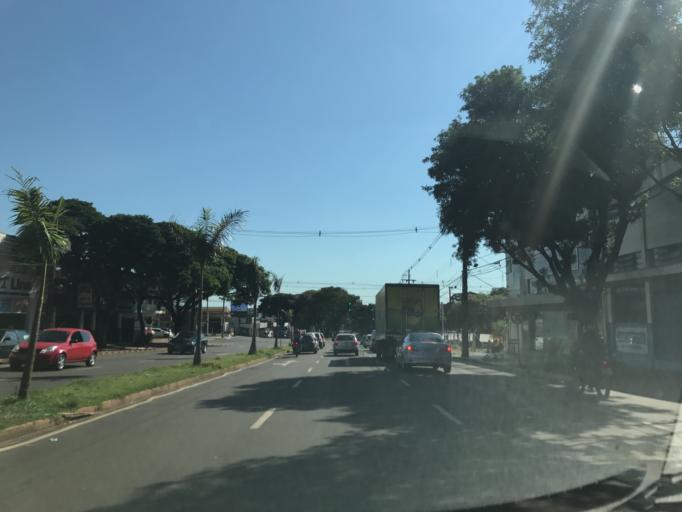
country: BR
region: Parana
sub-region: Maringa
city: Maringa
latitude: -23.4169
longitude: -51.9544
